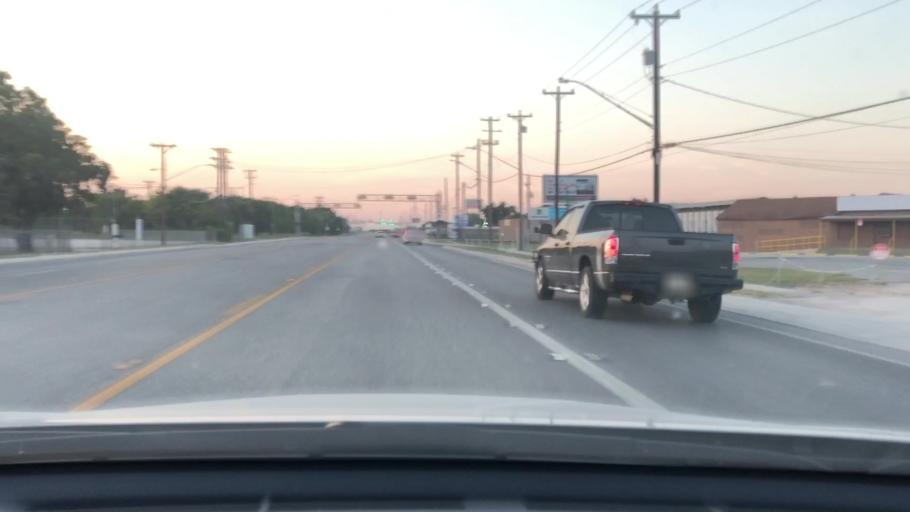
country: US
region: Texas
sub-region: Bexar County
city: Kirby
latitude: 29.4373
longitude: -98.4054
